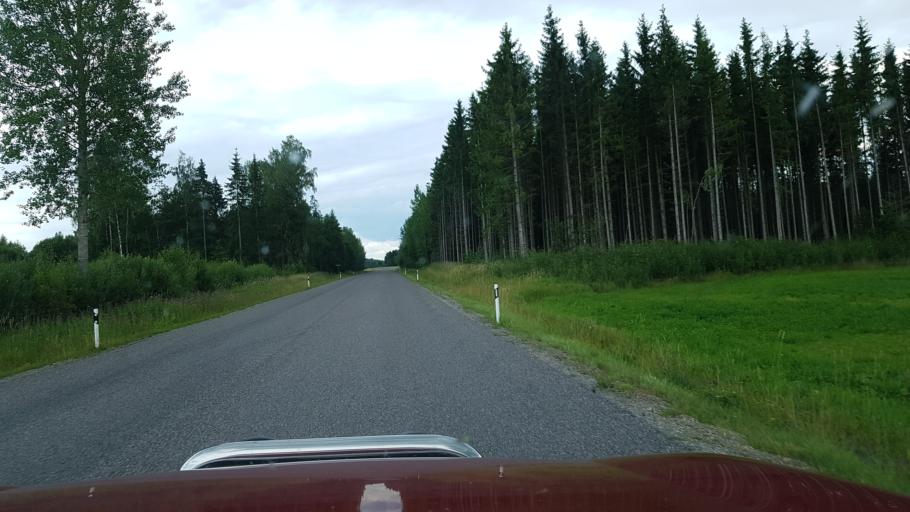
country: EE
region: Polvamaa
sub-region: Raepina vald
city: Rapina
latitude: 58.1229
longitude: 27.2837
